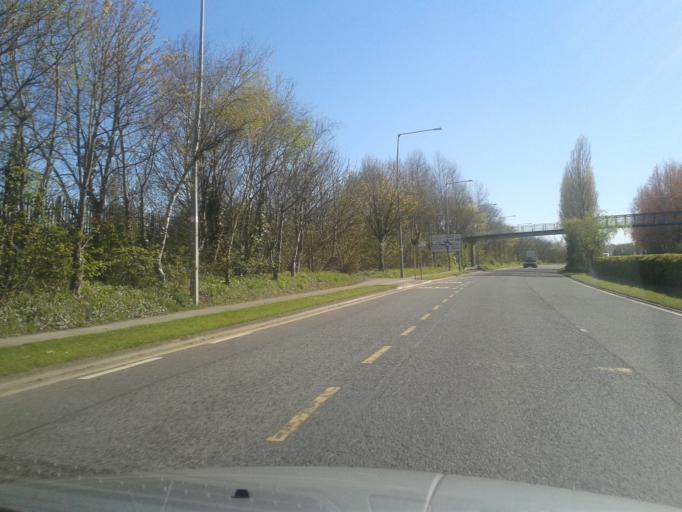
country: IE
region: Leinster
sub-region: Fingal County
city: Swords
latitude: 53.4574
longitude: -6.2124
